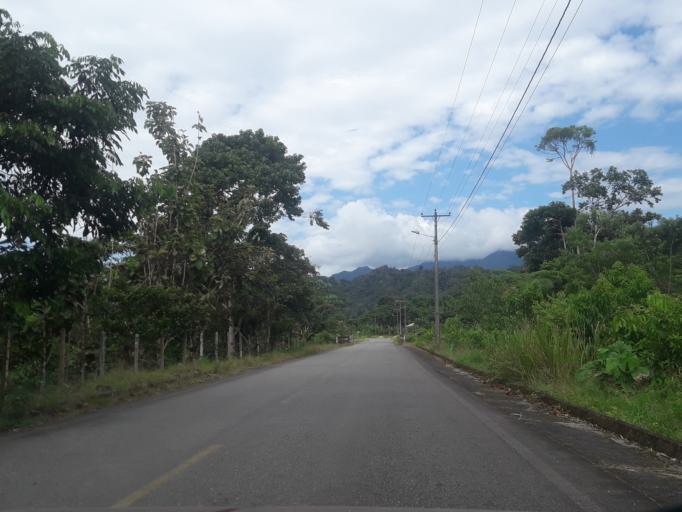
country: EC
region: Napo
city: Tena
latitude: -1.0611
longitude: -77.9024
